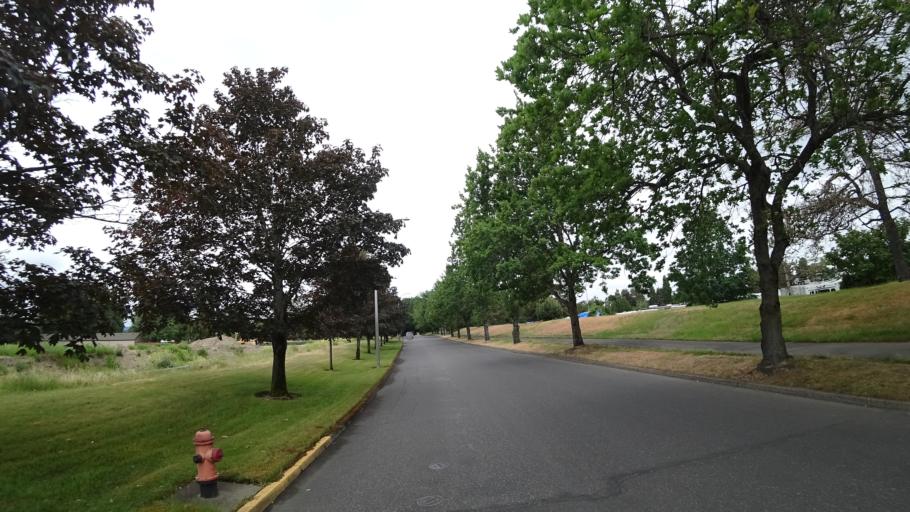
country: US
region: Washington
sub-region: Clark County
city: Vancouver
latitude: 45.6057
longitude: -122.6663
